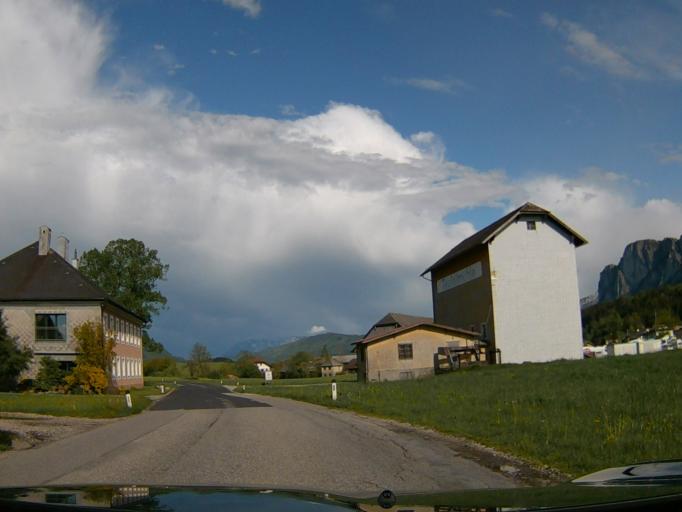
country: AT
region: Salzburg
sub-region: Politischer Bezirk Salzburg-Umgebung
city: Fuschl am See
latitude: 47.8372
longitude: 13.3024
